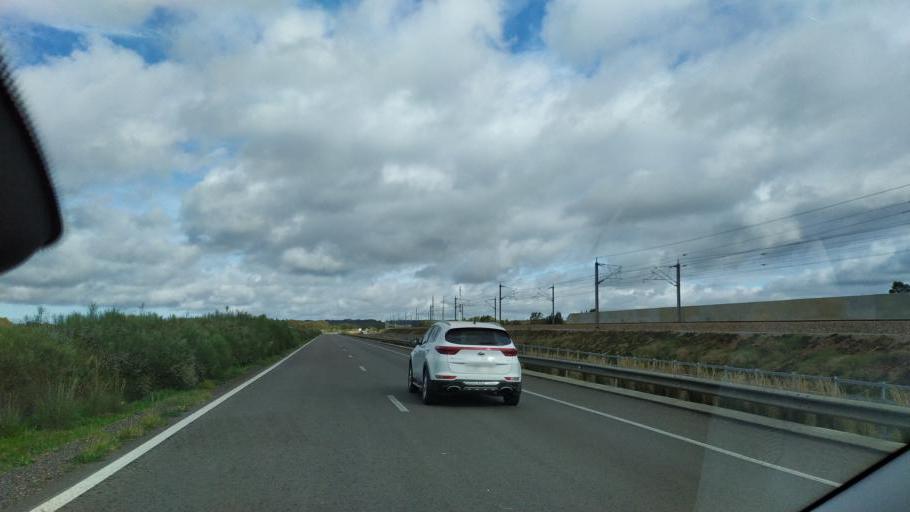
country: MA
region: Gharb-Chrarda-Beni Hssen
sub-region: Kenitra Province
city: Lalla Mimouna
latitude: 34.8960
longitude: -6.2094
